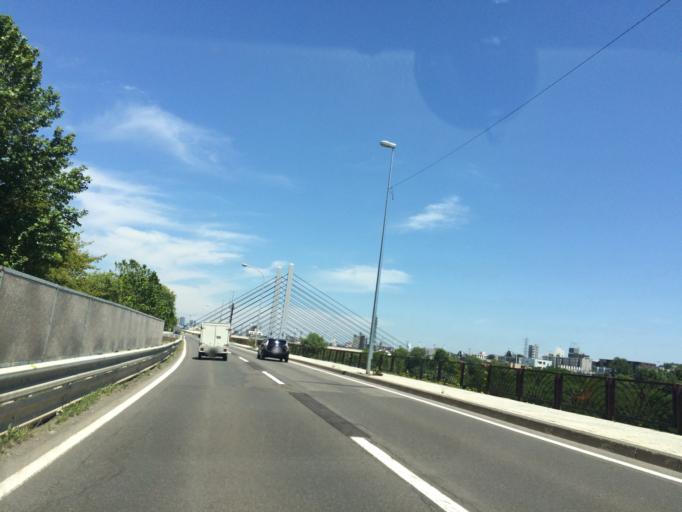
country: JP
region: Hokkaido
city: Sapporo
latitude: 43.0136
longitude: 141.3517
